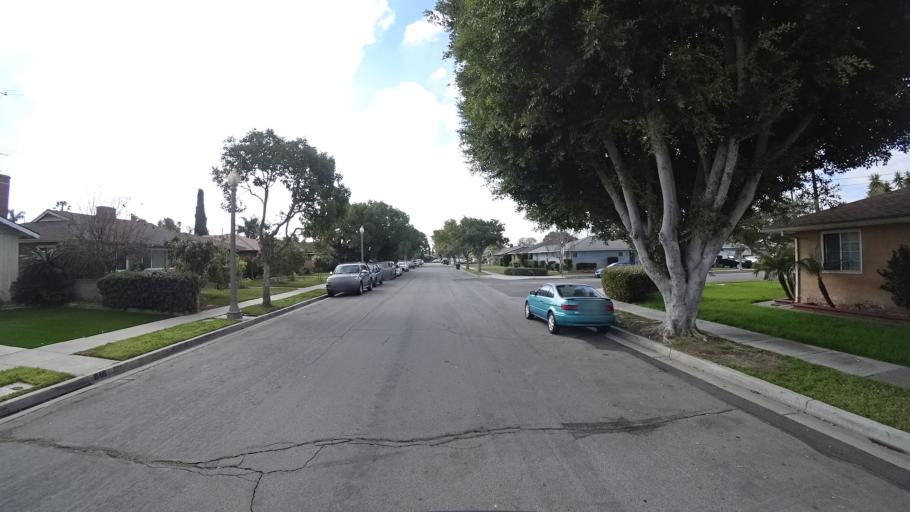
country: US
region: California
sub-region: Orange County
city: Anaheim
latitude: 33.8254
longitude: -117.9139
